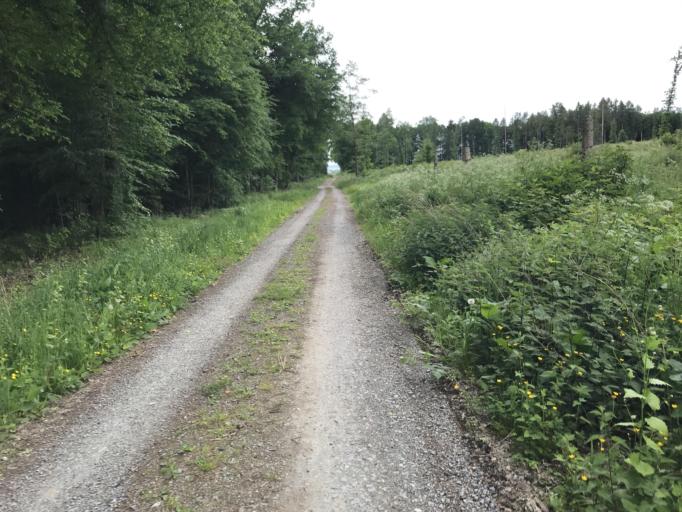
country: DE
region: Hesse
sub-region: Regierungsbezirk Kassel
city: Martinhagen
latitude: 51.2973
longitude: 9.2553
